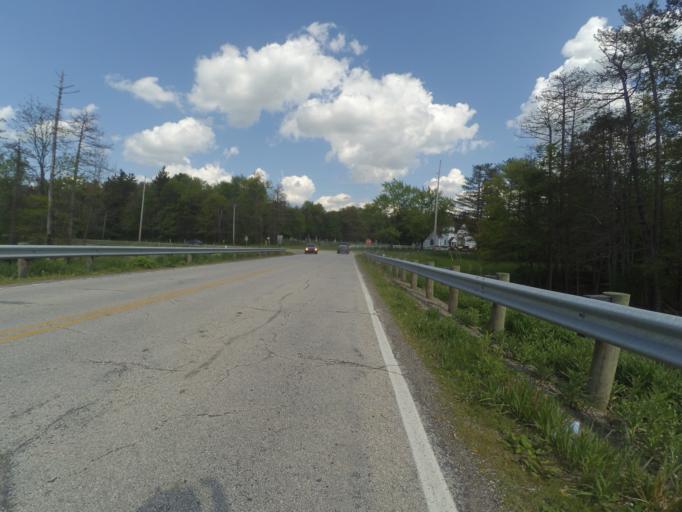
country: US
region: Ohio
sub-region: Trumbull County
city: Mineral Ridge
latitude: 41.1354
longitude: -80.7913
